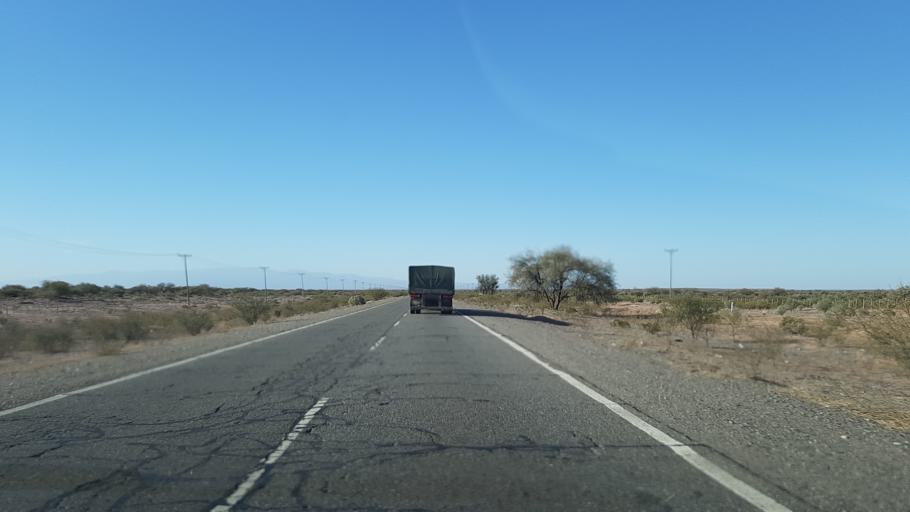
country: AR
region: San Juan
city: Caucete
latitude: -31.6544
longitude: -67.7692
